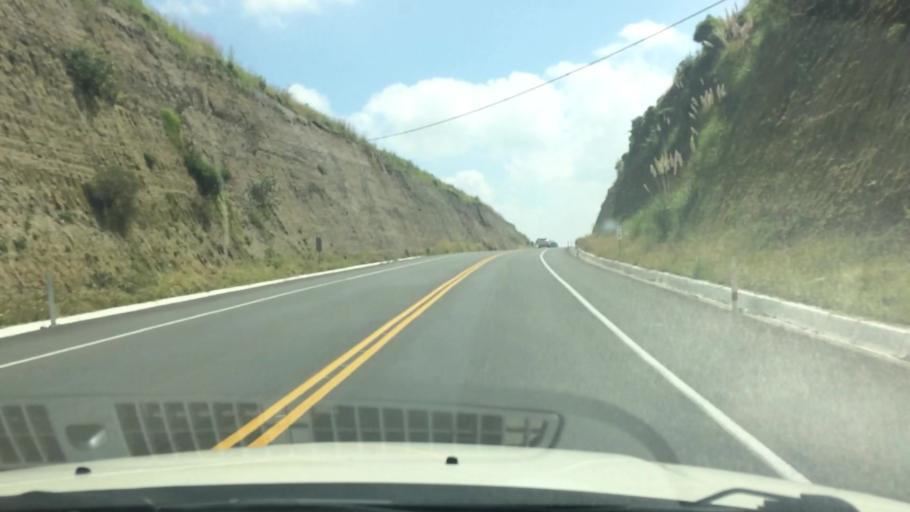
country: MX
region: Mexico
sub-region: Almoloya de Juarez
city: San Pedro de la Hortaliza (Ejido Almoloyan)
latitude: 19.3788
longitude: -99.8600
